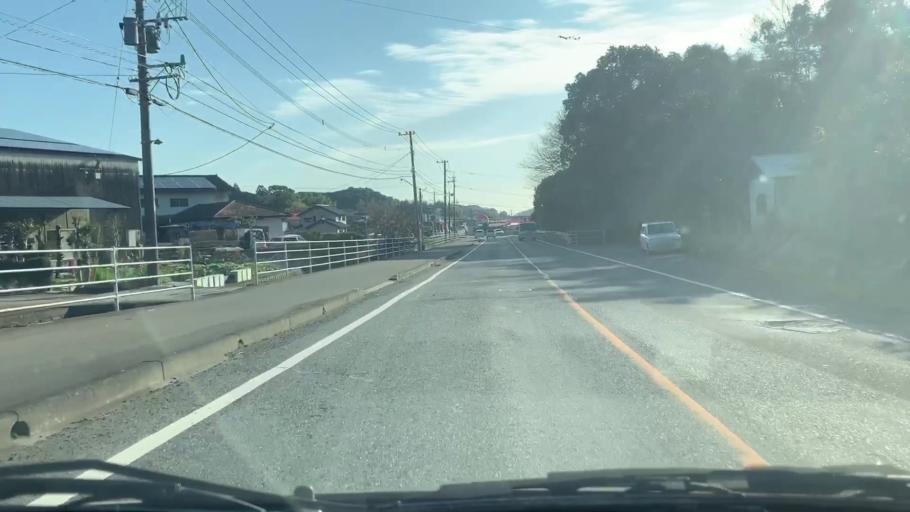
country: JP
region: Saga Prefecture
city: Takeocho-takeo
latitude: 33.2263
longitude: 130.0398
